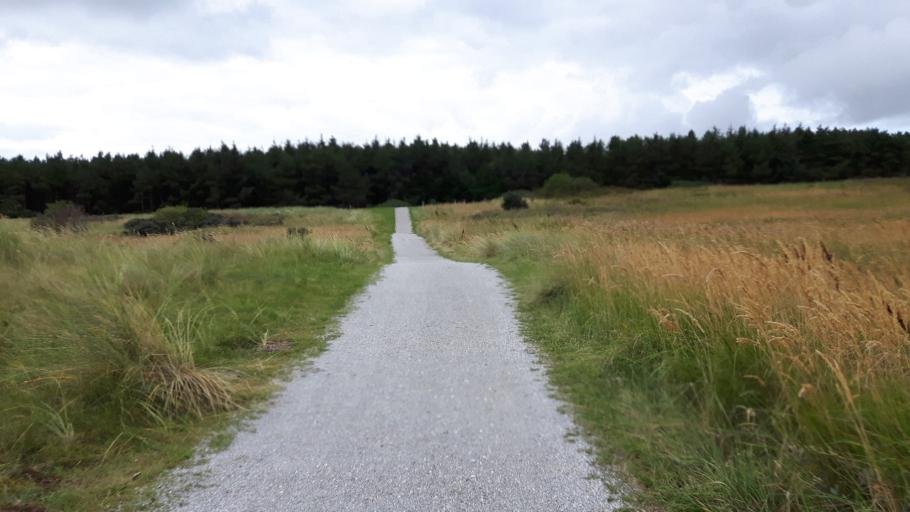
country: NL
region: Friesland
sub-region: Gemeente Ameland
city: Nes
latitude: 53.4538
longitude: 5.7151
